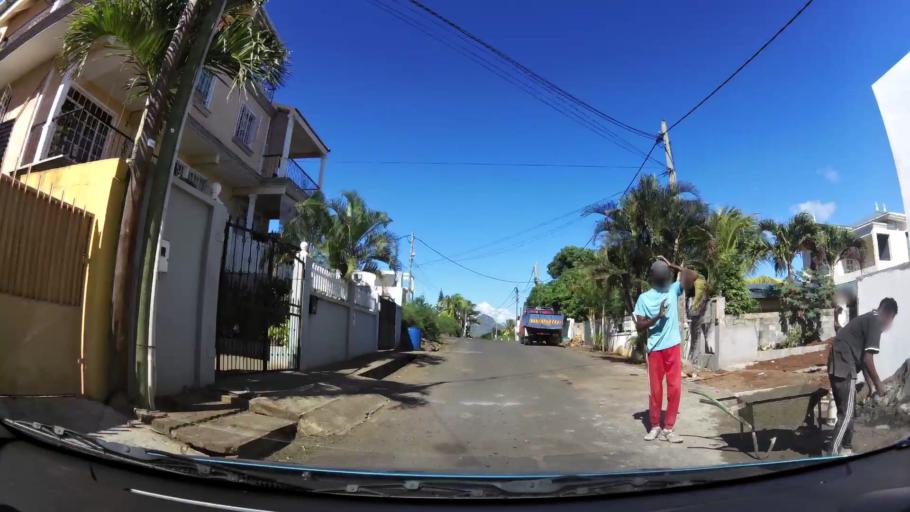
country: MU
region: Black River
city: Flic en Flac
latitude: -20.2780
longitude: 57.3758
